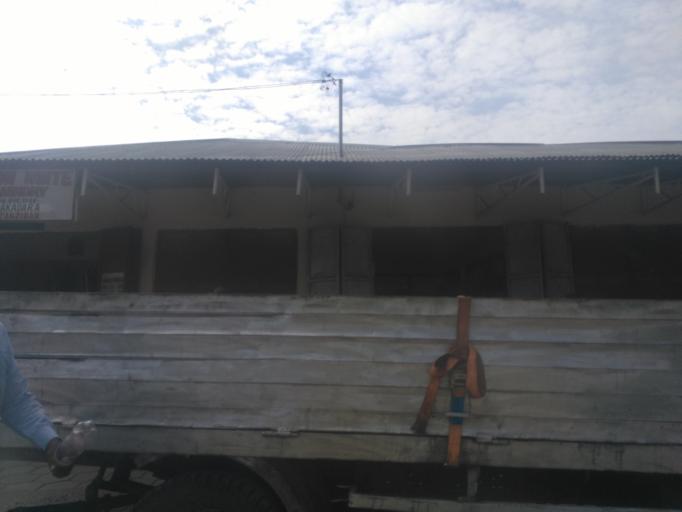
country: TZ
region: Zanzibar Urban/West
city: Zanzibar
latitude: -6.1586
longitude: 39.2051
